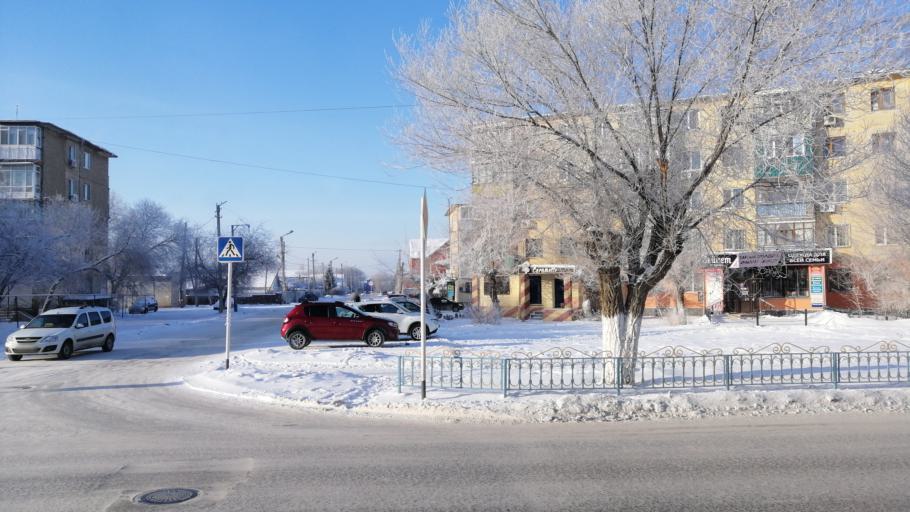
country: KZ
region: Aqtoebe
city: Aqtobe
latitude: 50.3069
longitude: 57.1497
